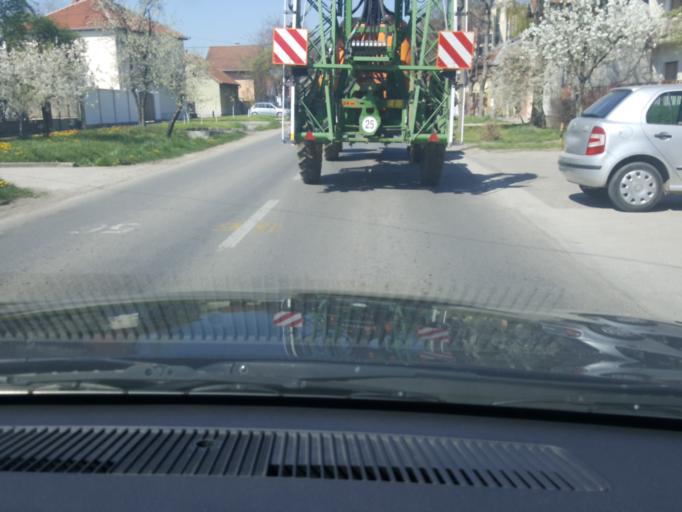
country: RS
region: Autonomna Pokrajina Vojvodina
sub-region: Zapadnobacki Okrug
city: Sombor
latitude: 45.7725
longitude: 19.1034
